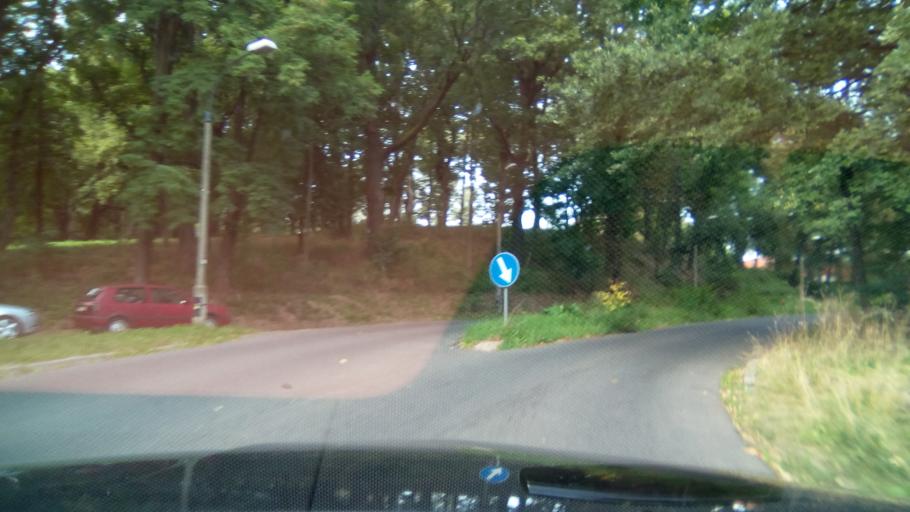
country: PL
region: Lesser Poland Voivodeship
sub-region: Krakow
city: Krakow
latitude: 50.0531
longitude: 19.8925
